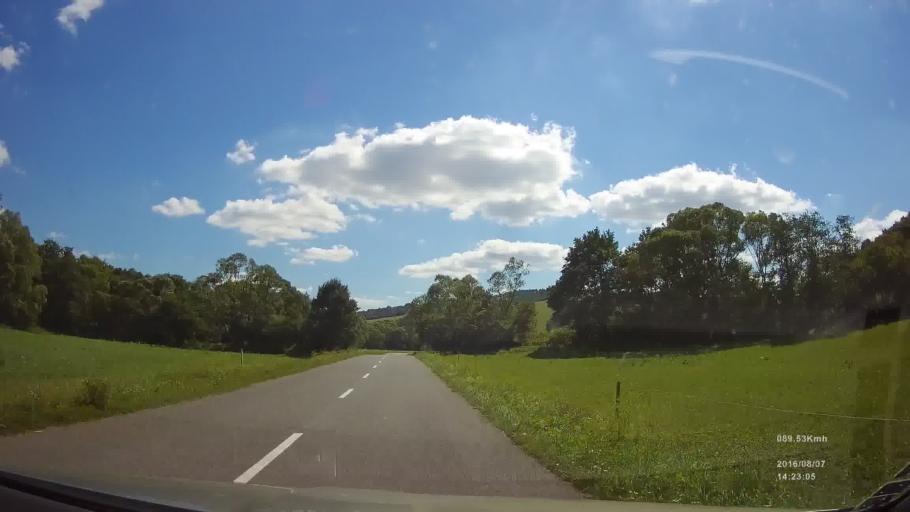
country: SK
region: Presovsky
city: Stropkov
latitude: 49.2675
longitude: 21.7482
